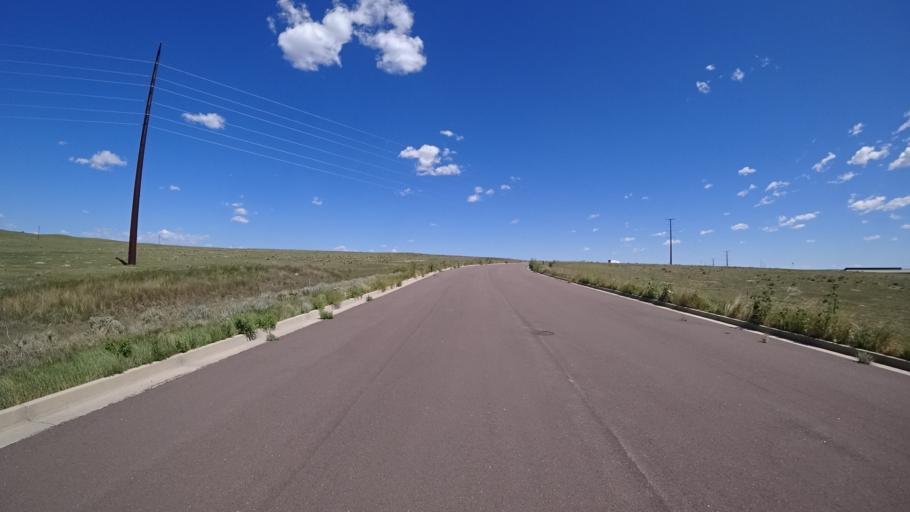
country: US
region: Colorado
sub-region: El Paso County
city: Security-Widefield
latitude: 38.7687
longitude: -104.6692
